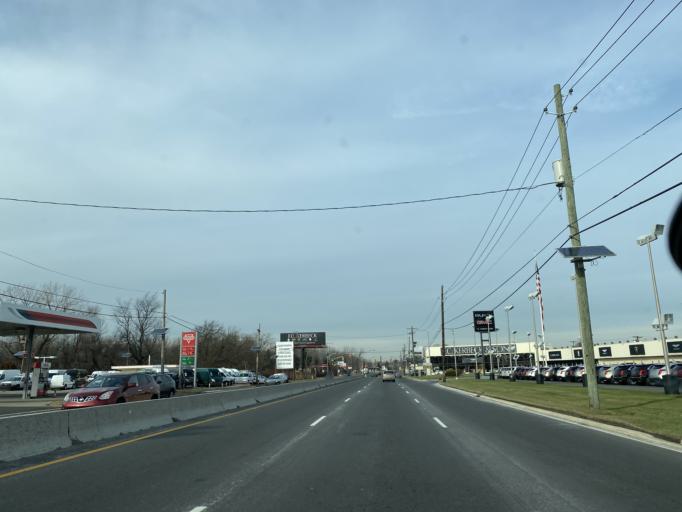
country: US
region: New Jersey
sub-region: Burlington County
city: Palmyra
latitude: 40.0002
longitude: -75.0360
